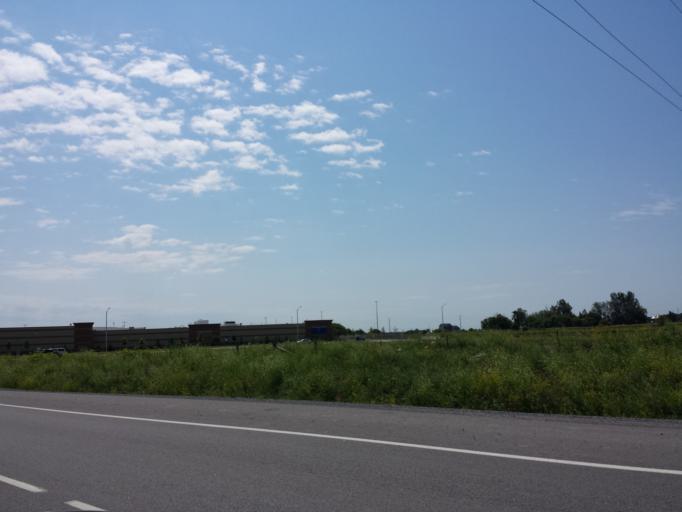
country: CA
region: Ontario
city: Bells Corners
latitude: 45.2768
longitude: -75.8747
